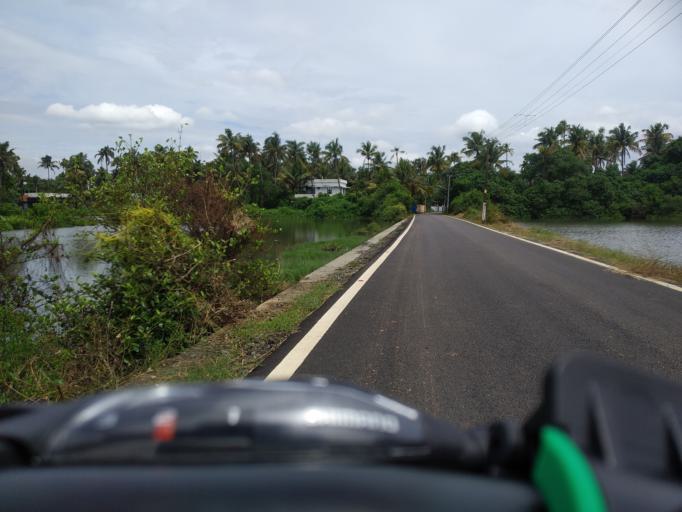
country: IN
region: Kerala
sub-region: Ernakulam
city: Elur
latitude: 10.0810
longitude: 76.2184
